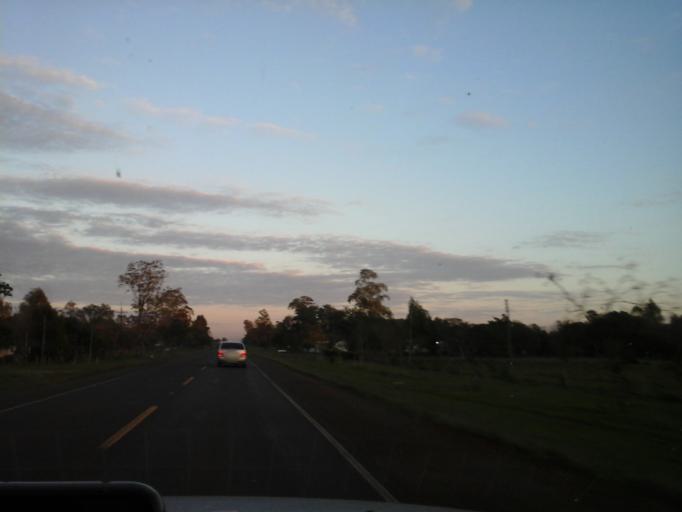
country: PY
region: Itapua
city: General Delgado
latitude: -27.0857
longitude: -56.5404
